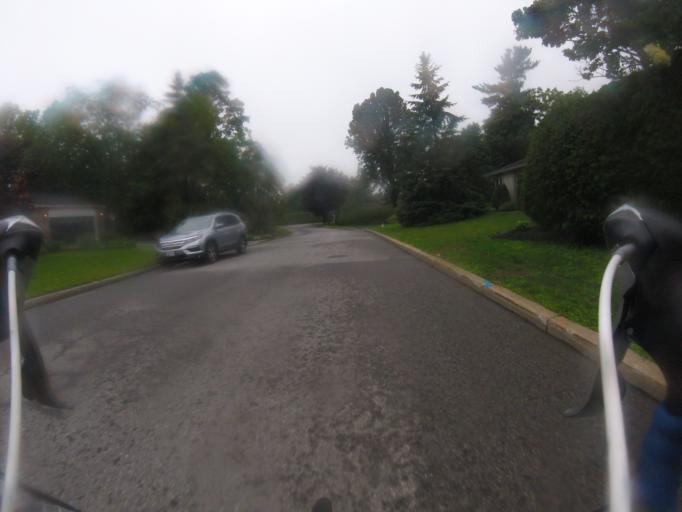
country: CA
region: Ontario
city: Bells Corners
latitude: 45.3364
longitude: -75.8011
